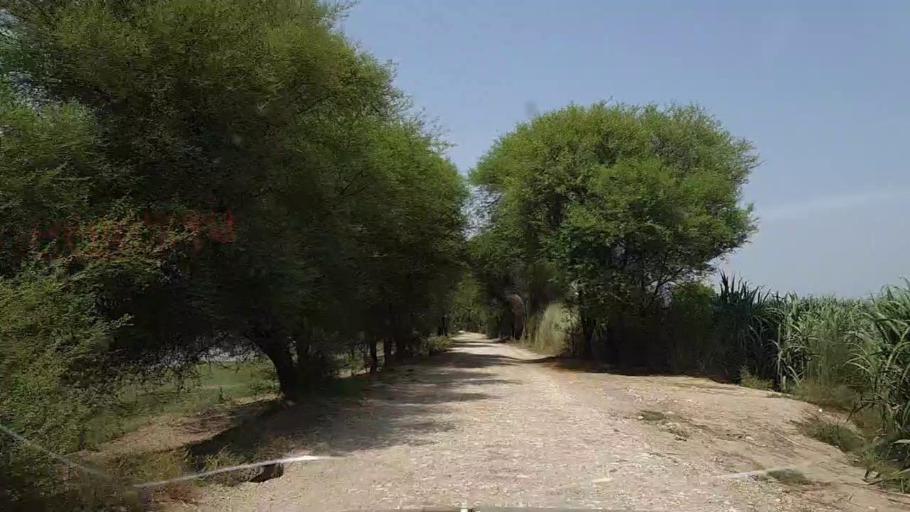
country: PK
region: Sindh
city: Ghotki
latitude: 28.0832
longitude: 69.3116
